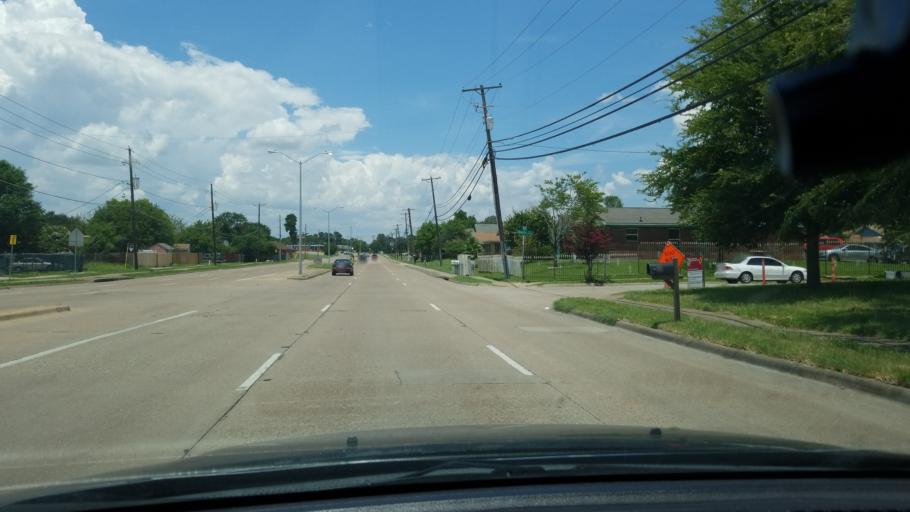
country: US
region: Texas
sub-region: Dallas County
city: Balch Springs
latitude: 32.7434
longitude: -96.6482
